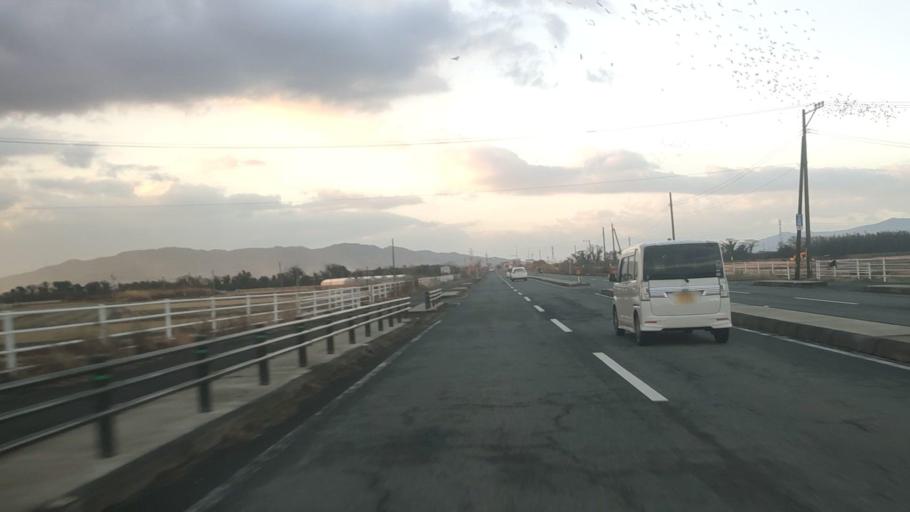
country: JP
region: Kumamoto
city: Kumamoto
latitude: 32.7468
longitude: 130.7068
